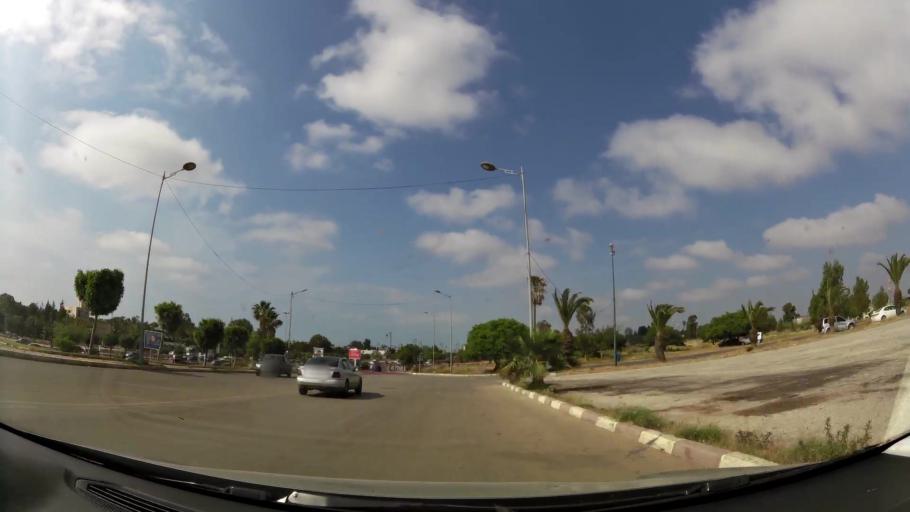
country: MA
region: Rabat-Sale-Zemmour-Zaer
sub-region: Rabat
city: Rabat
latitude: 33.9753
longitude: -6.8619
